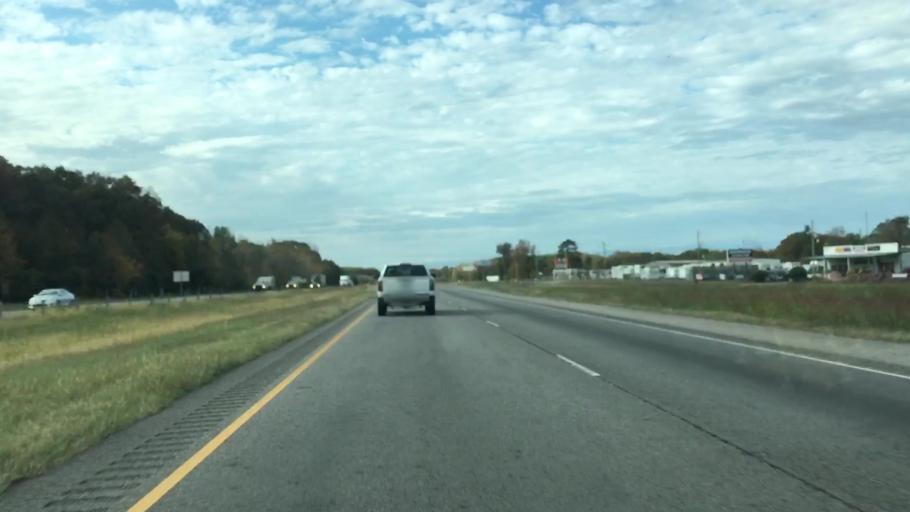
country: US
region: Arkansas
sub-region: Pope County
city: Atkins
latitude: 35.2208
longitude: -92.8317
